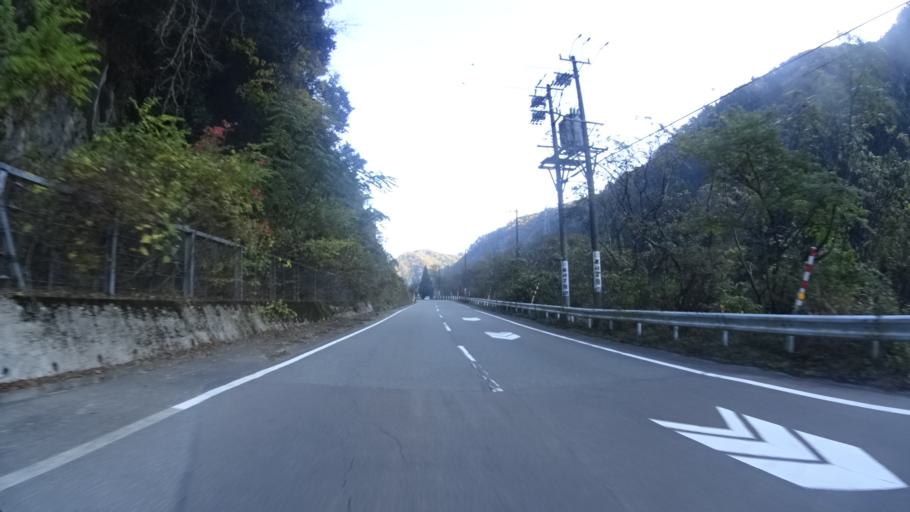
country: JP
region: Fukui
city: Maruoka
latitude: 36.2017
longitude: 136.3453
